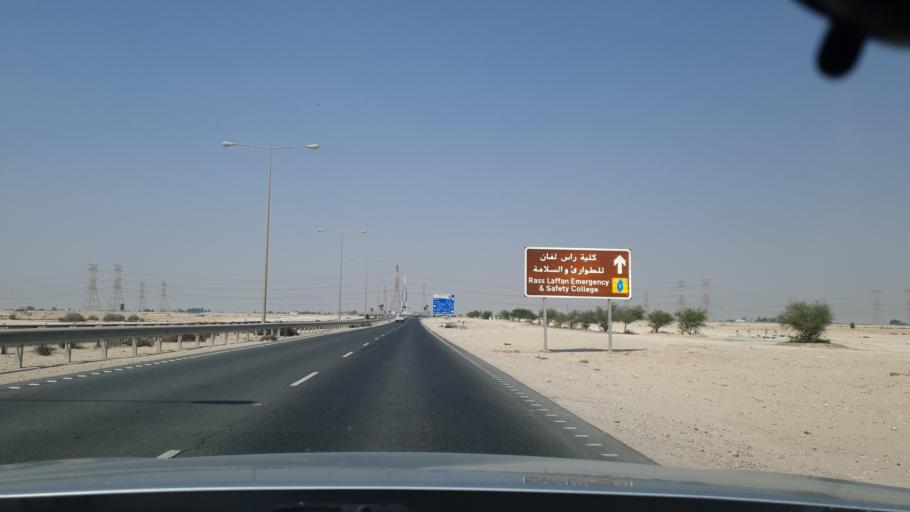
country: QA
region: Al Khawr
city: Al Khawr
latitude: 25.7498
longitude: 51.4786
